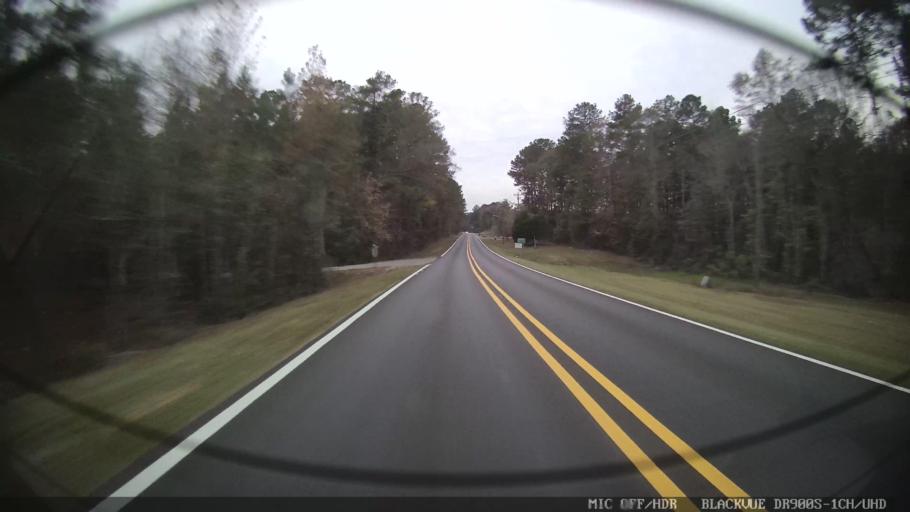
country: US
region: Mississippi
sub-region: Clarke County
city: Quitman
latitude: 32.0456
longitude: -88.6982
